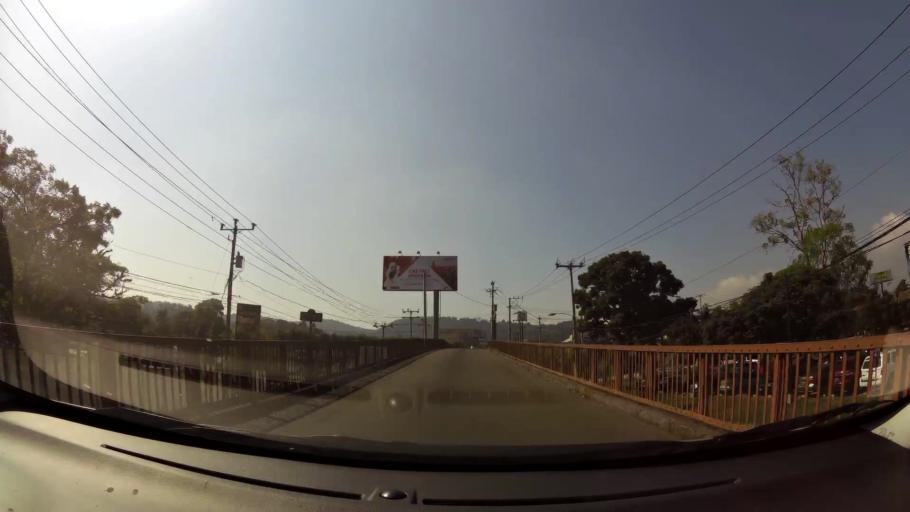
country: SV
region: La Libertad
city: Antiguo Cuscatlan
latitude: 13.6753
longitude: -89.2528
